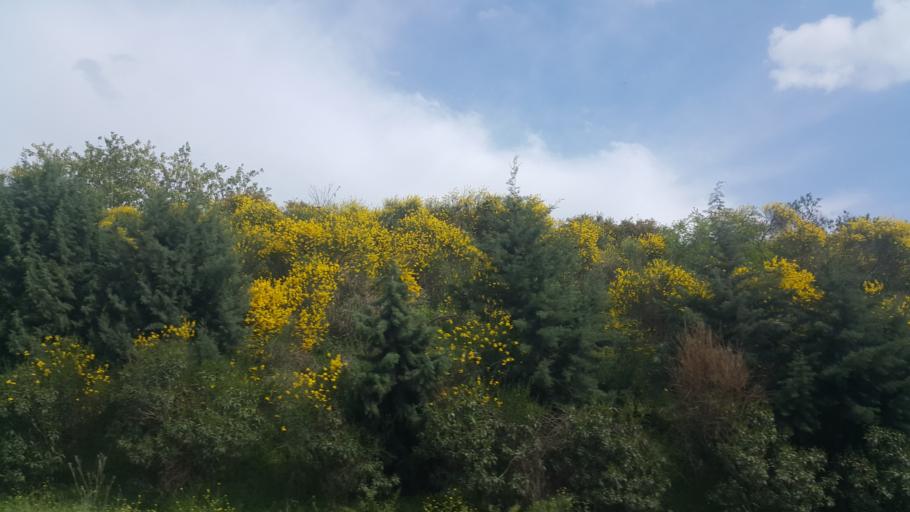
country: TR
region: Mersin
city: Kazanli
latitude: 36.9322
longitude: 34.7112
